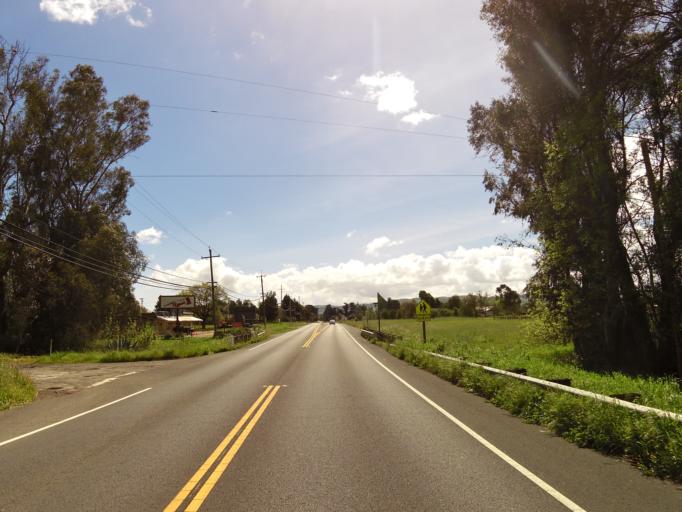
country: US
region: California
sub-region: Sonoma County
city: Sonoma
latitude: 38.2720
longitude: -122.4610
